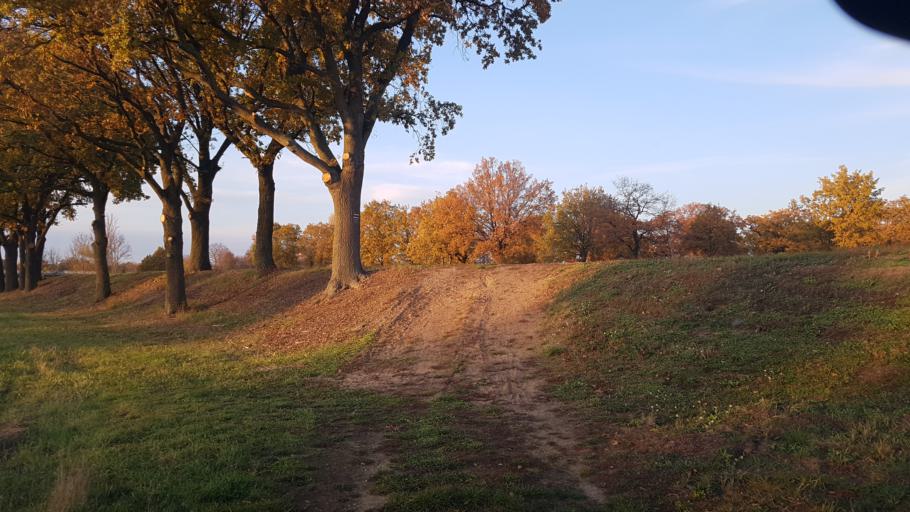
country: DE
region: Brandenburg
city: Schilda
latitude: 51.6038
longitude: 13.3153
